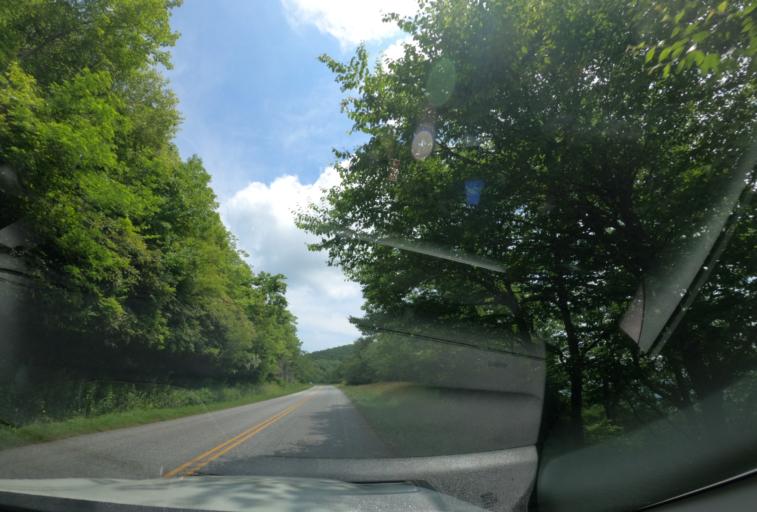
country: US
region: North Carolina
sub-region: Haywood County
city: Canton
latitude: 35.3937
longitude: -82.7704
